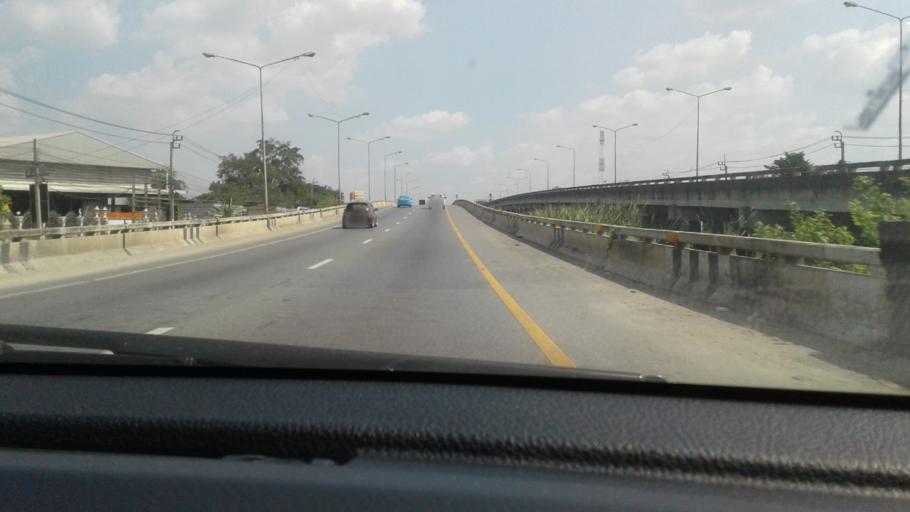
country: TH
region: Nonthaburi
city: Bang Bua Thong
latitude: 13.9480
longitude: 100.4427
